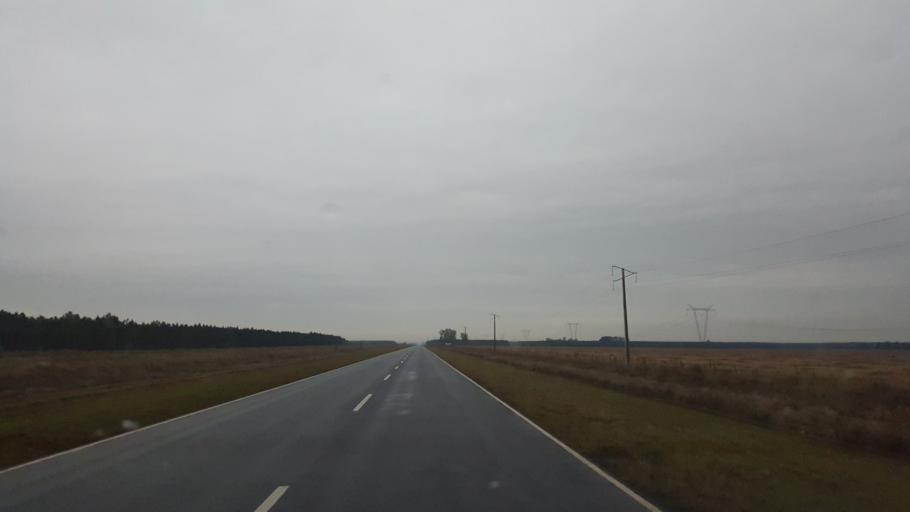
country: PY
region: Itapua
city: San Cosme y Damian
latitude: -27.5704
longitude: -56.2703
